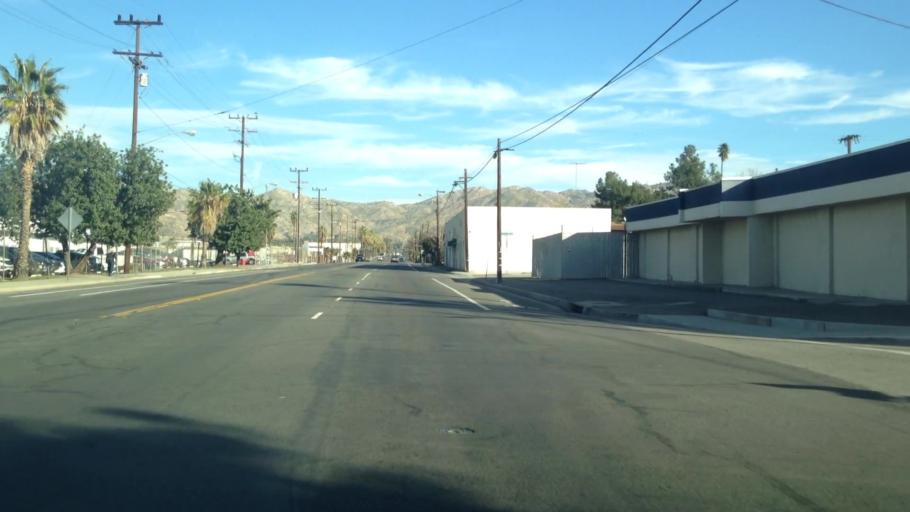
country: US
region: California
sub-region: Riverside County
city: Highgrove
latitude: 33.9829
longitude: -117.3618
